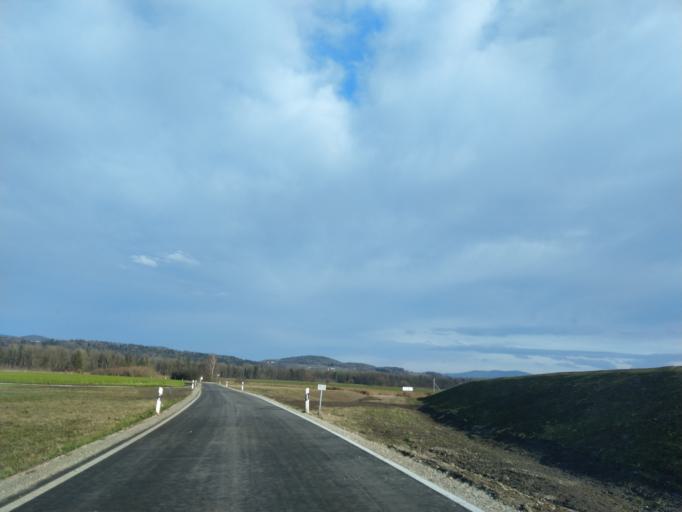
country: DE
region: Bavaria
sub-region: Lower Bavaria
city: Moos
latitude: 48.7837
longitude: 12.9690
